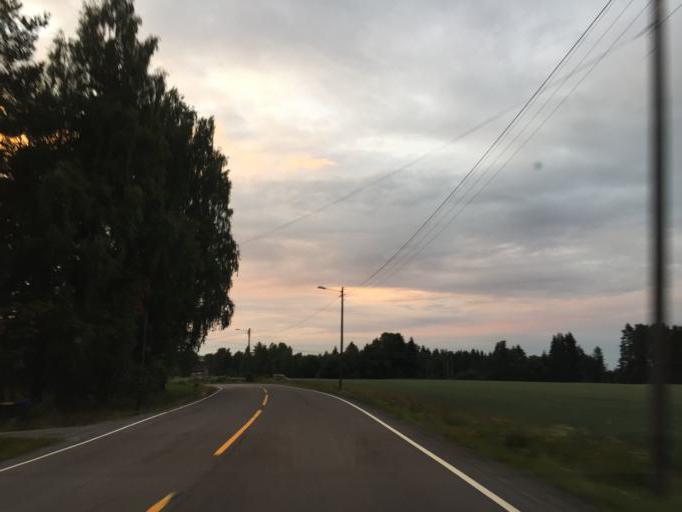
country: NO
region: Akershus
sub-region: Nes
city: Auli
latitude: 60.0516
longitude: 11.3784
